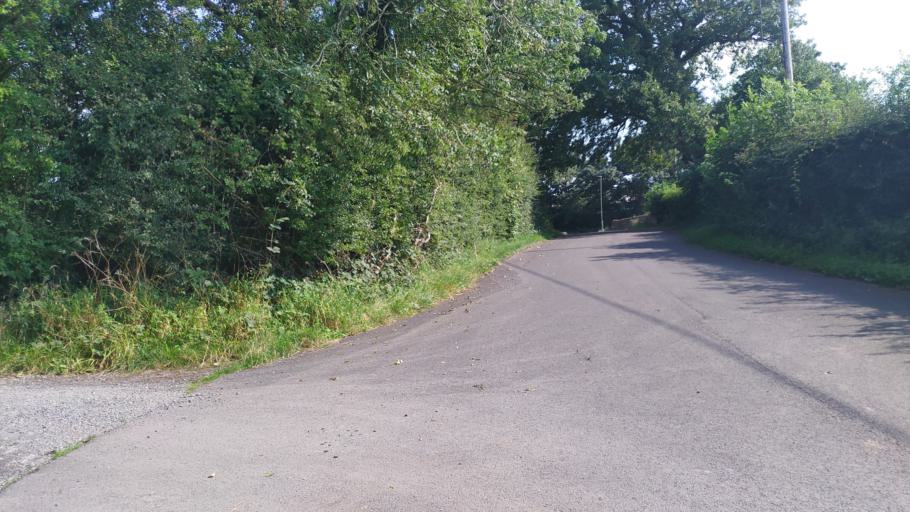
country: GB
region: England
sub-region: Lancashire
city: Clayton-le-Woods
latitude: 53.7207
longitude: -2.6330
